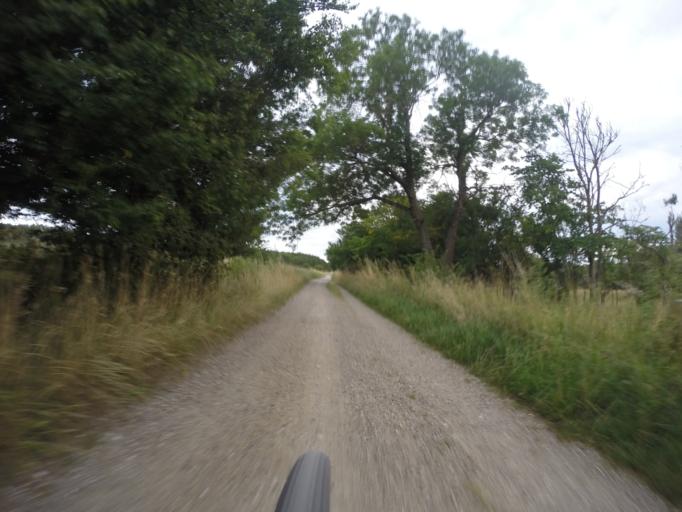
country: DK
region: Capital Region
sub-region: Hoje-Taastrup Kommune
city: Taastrup
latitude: 55.6919
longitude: 12.3179
